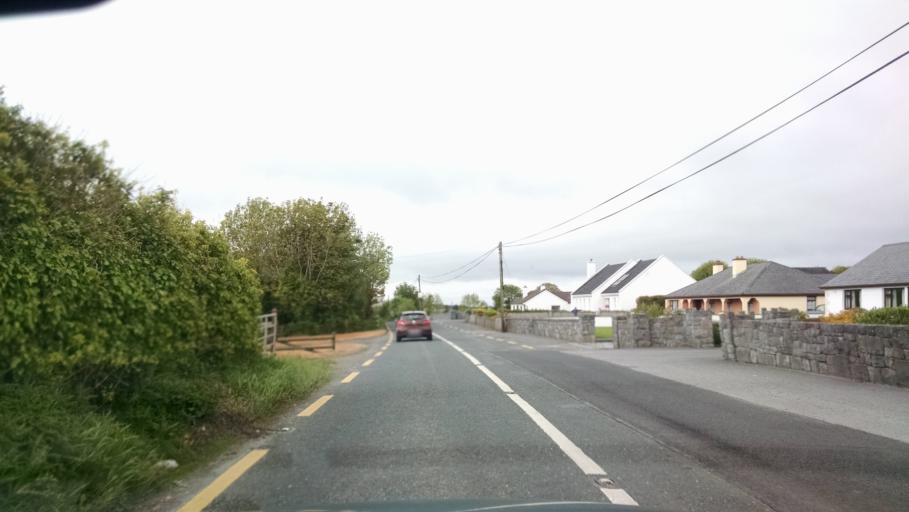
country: IE
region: Connaught
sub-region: County Galway
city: Moycullen
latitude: 53.4812
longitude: -9.0895
